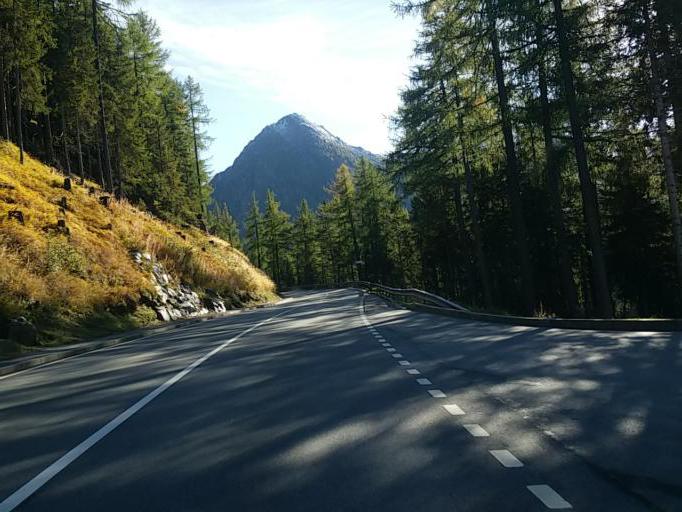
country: CH
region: Valais
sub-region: Brig District
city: Brig
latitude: 46.2828
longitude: 8.0373
